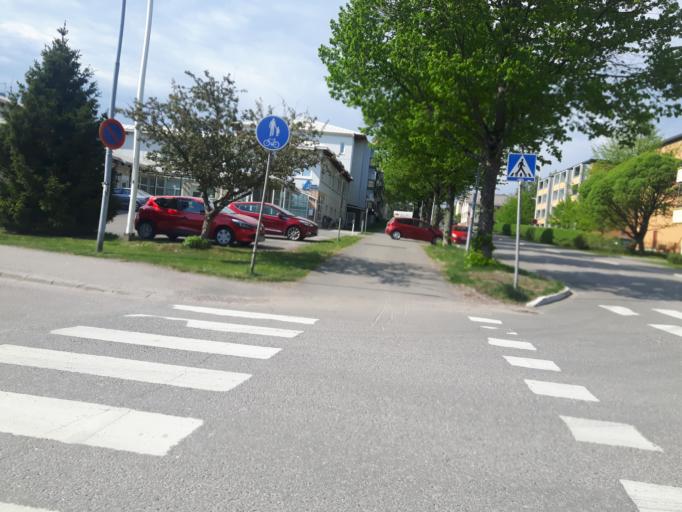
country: FI
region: Uusimaa
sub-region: Porvoo
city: Porvoo
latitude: 60.3954
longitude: 25.6727
